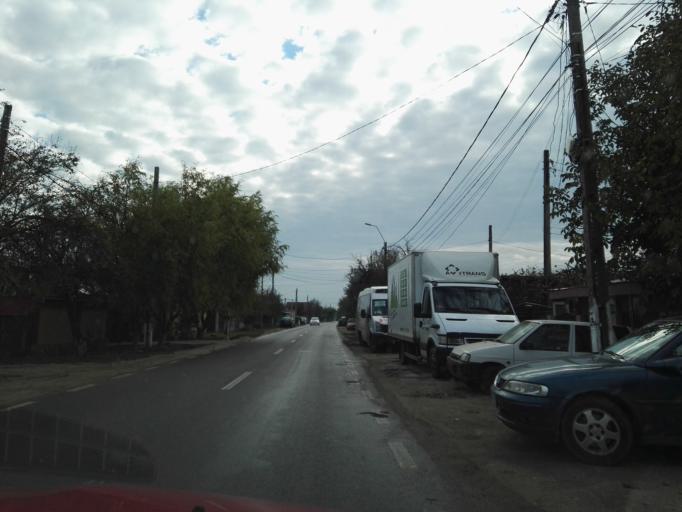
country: RO
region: Ilfov
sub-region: Comuna Magurele
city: Magurele
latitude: 44.3431
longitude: 26.0432
